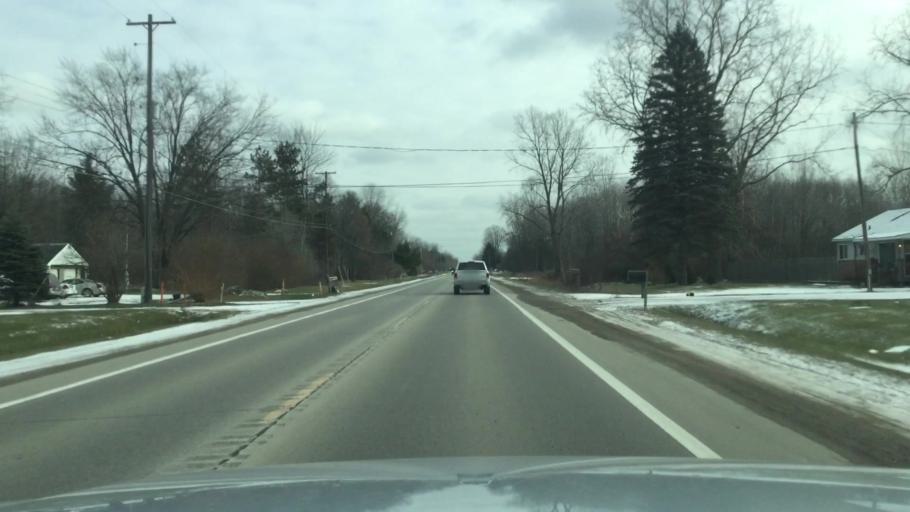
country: US
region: Michigan
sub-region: Genesee County
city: Clio
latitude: 43.1770
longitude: -83.8094
